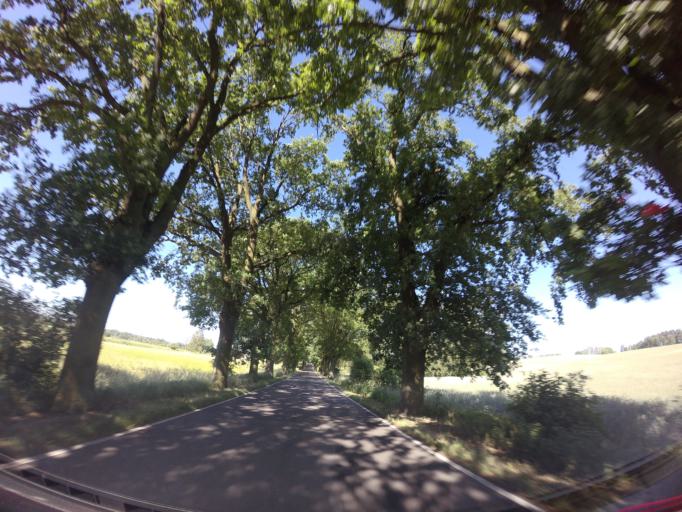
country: PL
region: West Pomeranian Voivodeship
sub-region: Powiat stargardzki
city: Dolice
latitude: 53.1965
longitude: 15.2256
